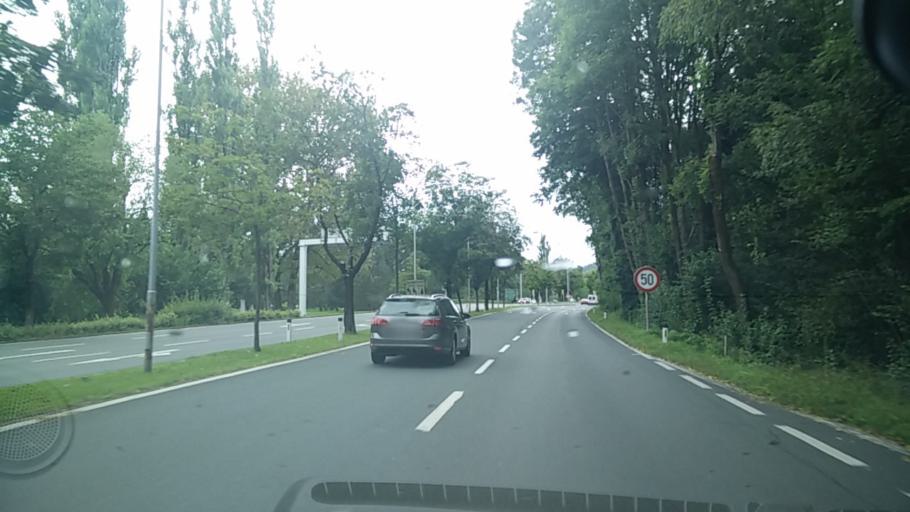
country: AT
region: Carinthia
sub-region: Klagenfurt am Woerthersee
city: Klagenfurt am Woerthersee
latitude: 46.6216
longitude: 14.2616
